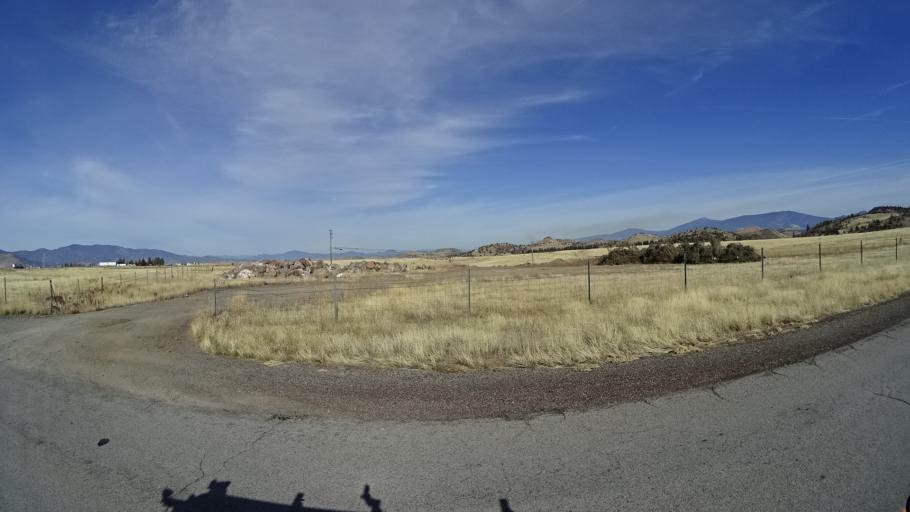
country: US
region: California
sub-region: Siskiyou County
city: Weed
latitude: 41.4720
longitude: -122.4492
